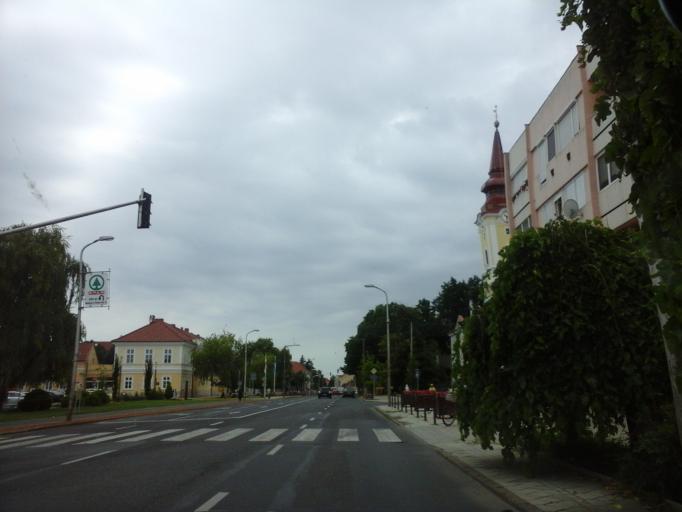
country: HU
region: Hajdu-Bihar
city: Hajduszoboszlo
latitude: 47.4440
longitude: 21.3900
